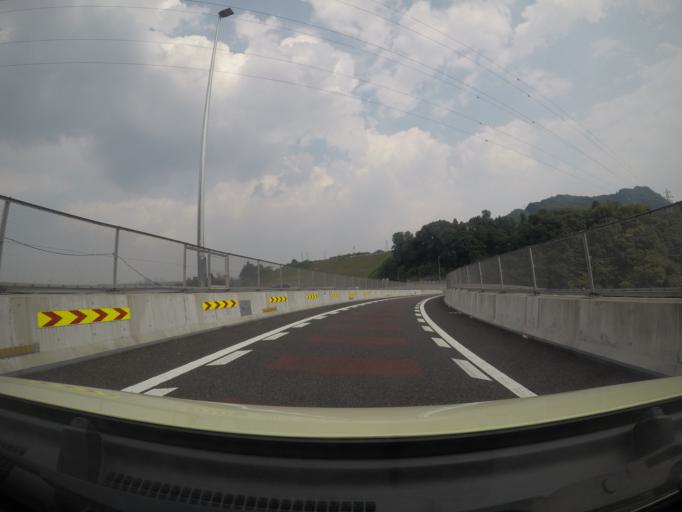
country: JP
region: Tokyo
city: Hachioji
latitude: 35.5802
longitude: 139.2892
